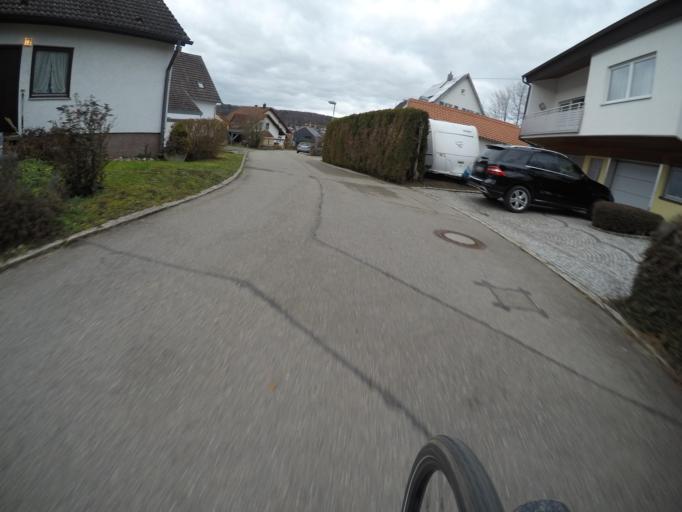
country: DE
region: Baden-Wuerttemberg
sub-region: Tuebingen Region
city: Wannweil
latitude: 48.5145
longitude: 9.1576
